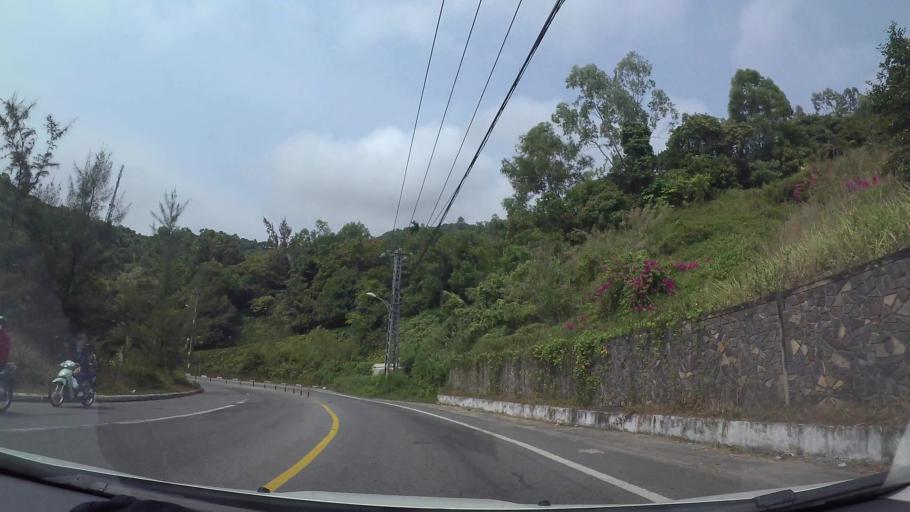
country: VN
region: Da Nang
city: Son Tra
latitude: 16.1003
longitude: 108.2755
